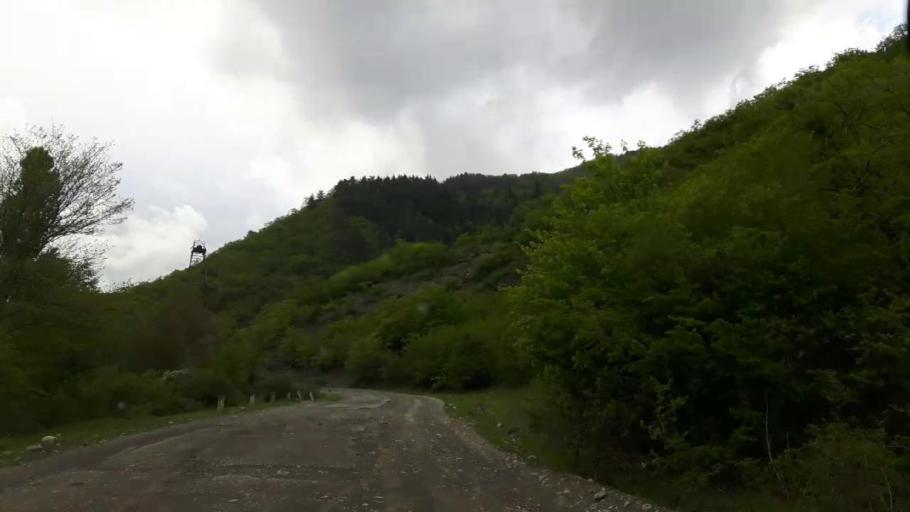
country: GE
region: Shida Kartli
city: Gori
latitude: 41.8787
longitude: 43.9910
